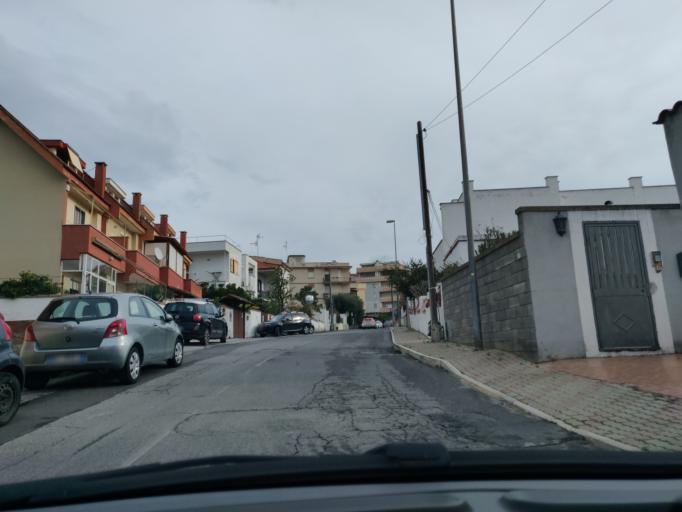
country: IT
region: Latium
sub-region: Citta metropolitana di Roma Capitale
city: Civitavecchia
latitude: 42.0962
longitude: 11.8100
